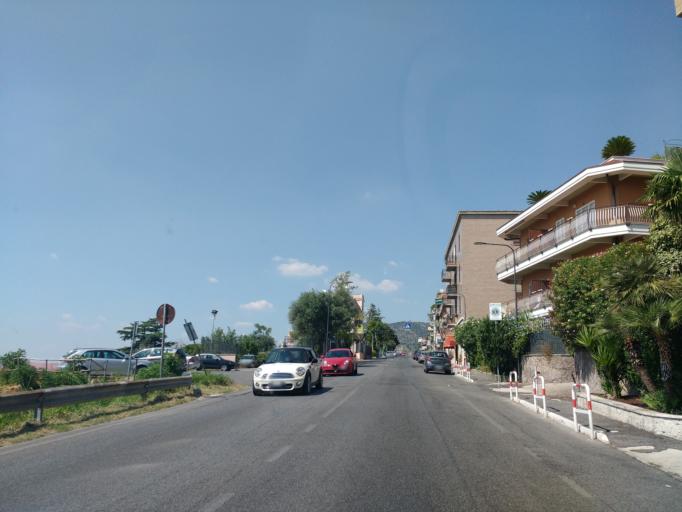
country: IT
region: Latium
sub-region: Citta metropolitana di Roma Capitale
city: Tivoli
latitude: 41.9532
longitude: 12.7914
